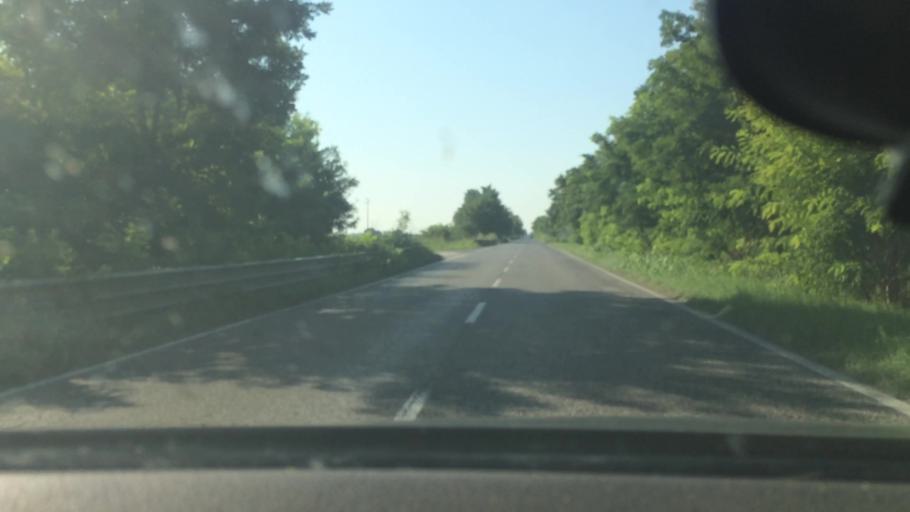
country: IT
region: Emilia-Romagna
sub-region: Provincia di Ferrara
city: Lagosanto
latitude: 44.7394
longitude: 12.1445
